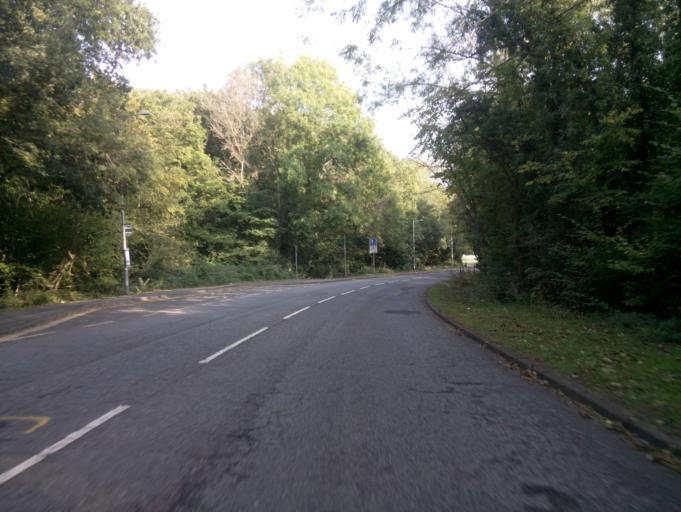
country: GB
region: Wales
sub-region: Torfaen County Borough
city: Cwmbran
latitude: 51.6587
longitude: -3.0337
